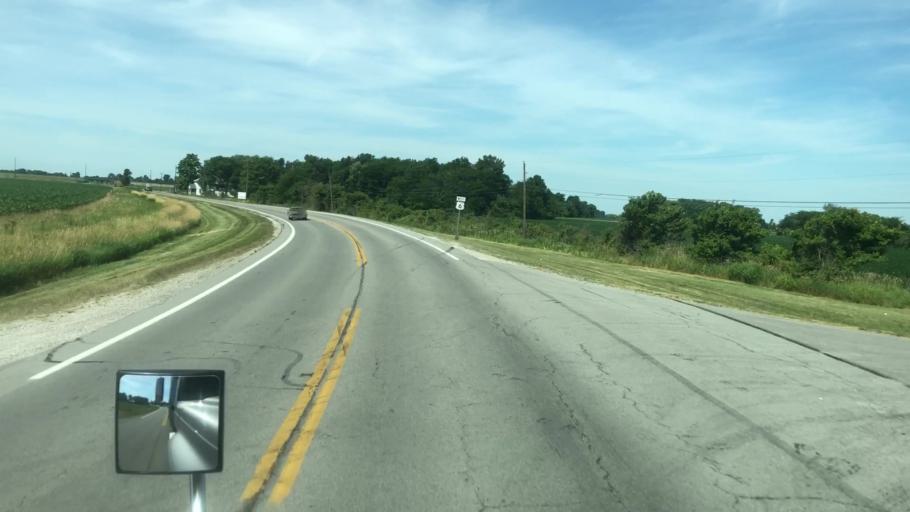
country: US
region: Ohio
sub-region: Sandusky County
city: Fremont
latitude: 41.3935
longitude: -83.0312
